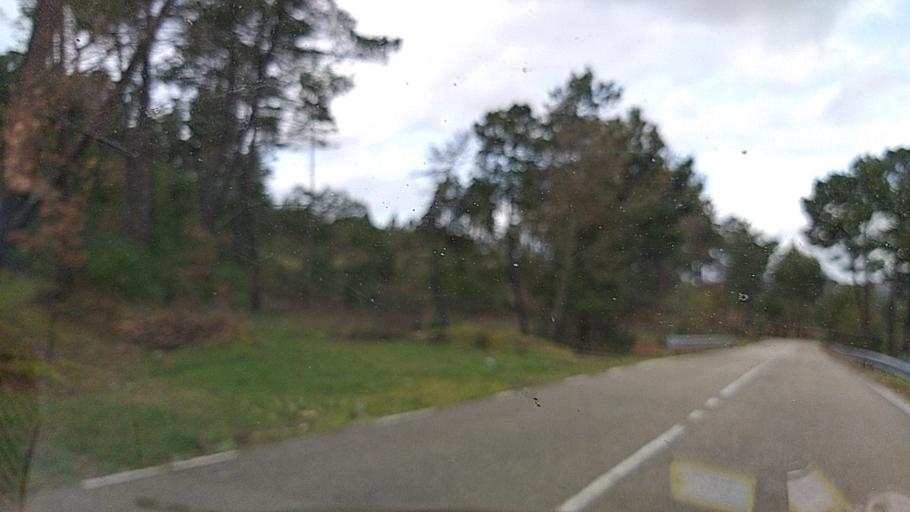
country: PT
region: Viseu
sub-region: Satao
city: Satao
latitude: 40.6595
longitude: -7.6634
